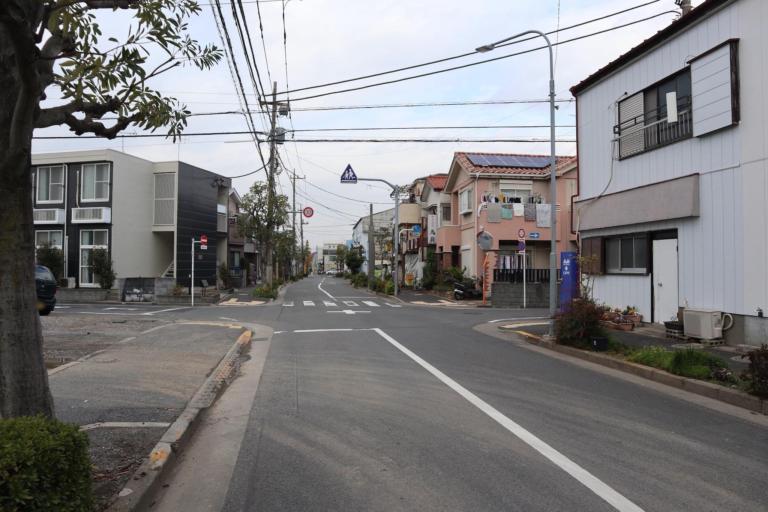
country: JP
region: Tokyo
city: Urayasu
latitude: 35.7085
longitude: 139.8766
